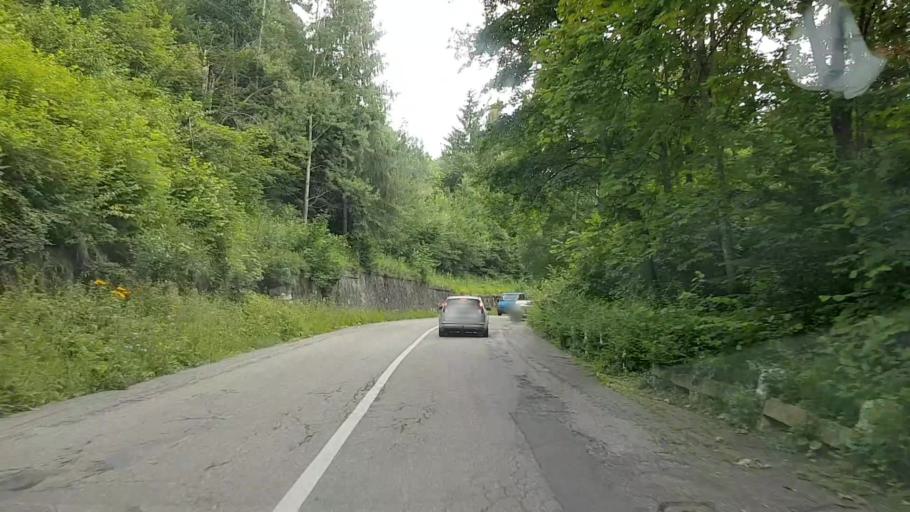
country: RO
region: Neamt
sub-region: Comuna Pangarati
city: Pangarati
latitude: 46.9453
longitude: 26.1265
